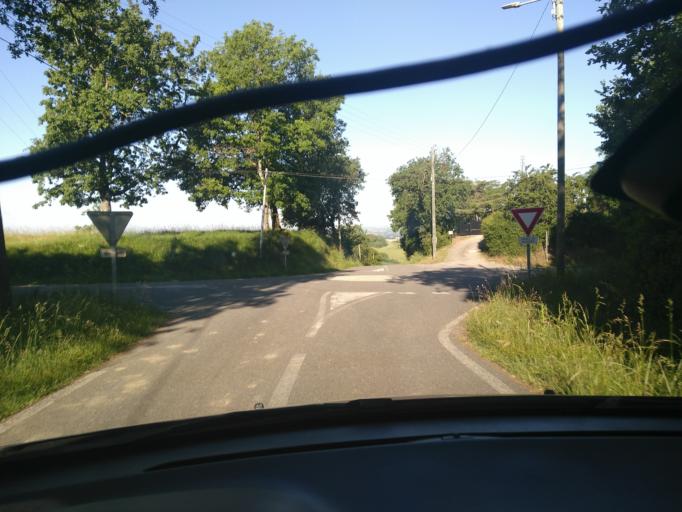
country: FR
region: Midi-Pyrenees
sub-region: Departement du Tarn-et-Garonne
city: Beaumont-de-Lomagne
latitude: 43.7836
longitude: 0.9993
